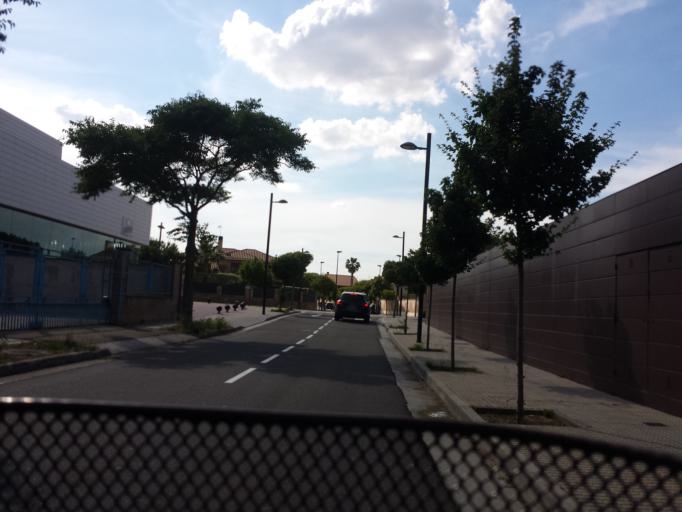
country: ES
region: Aragon
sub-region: Provincia de Zaragoza
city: Delicias
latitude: 41.6287
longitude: -0.9128
